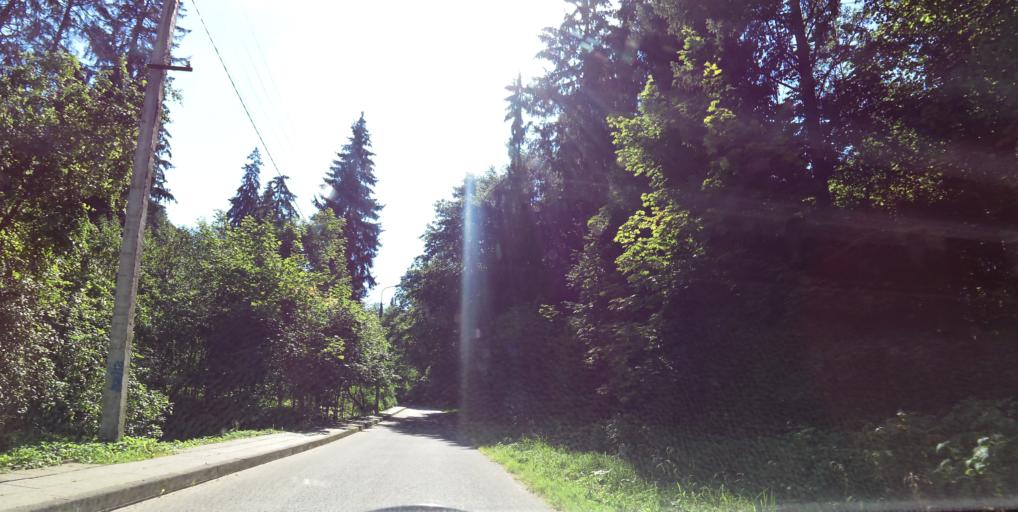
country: LT
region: Vilnius County
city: Rasos
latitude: 54.6750
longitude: 25.3566
